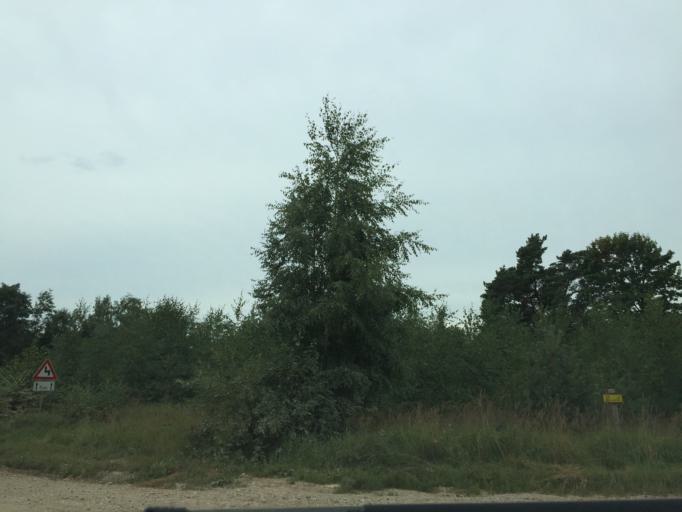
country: LV
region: Jaunpils
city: Jaunpils
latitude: 56.7494
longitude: 23.1231
